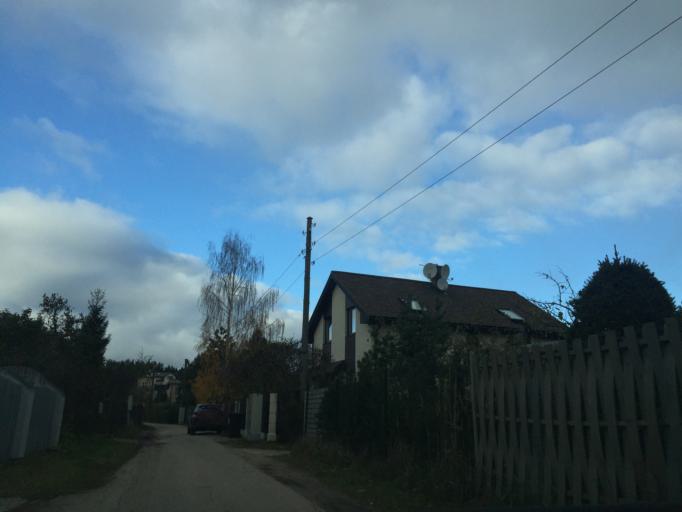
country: LV
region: Carnikava
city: Carnikava
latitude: 57.1516
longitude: 24.2827
